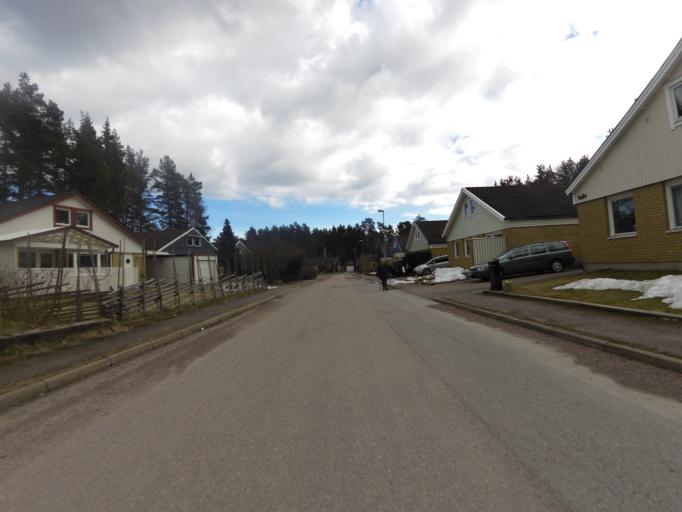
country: SE
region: Gaevleborg
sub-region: Gavle Kommun
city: Gavle
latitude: 60.6964
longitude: 17.0982
